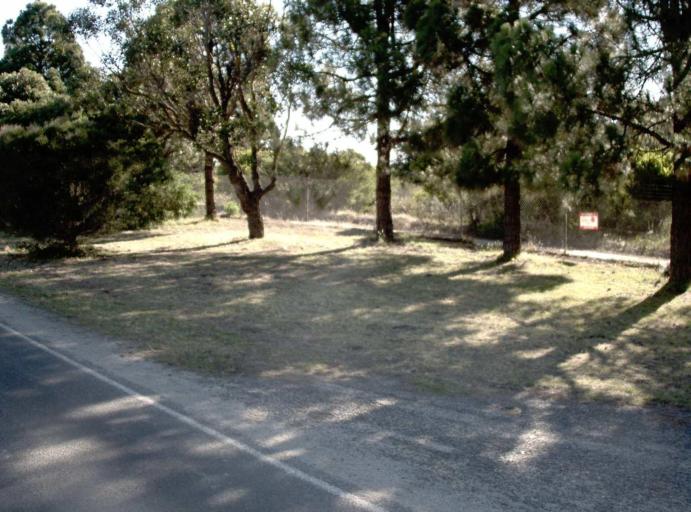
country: AU
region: Victoria
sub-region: Latrobe
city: Morwell
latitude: -38.7077
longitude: 146.3973
